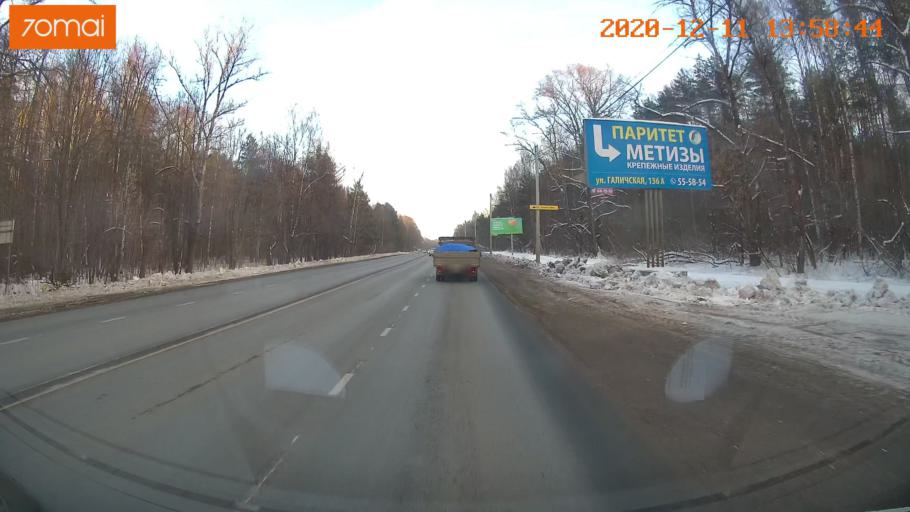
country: RU
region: Kostroma
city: Oktyabr'skiy
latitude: 57.7819
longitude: 40.9992
